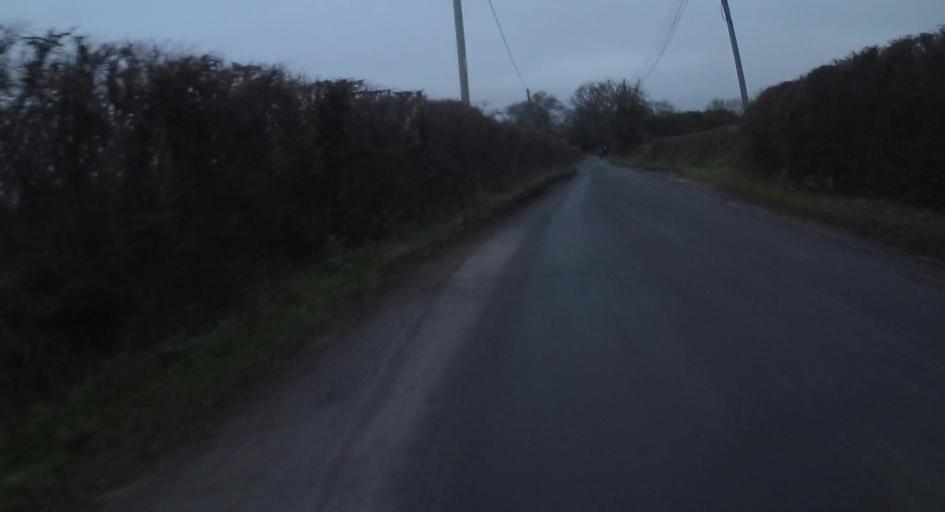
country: GB
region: England
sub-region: Hampshire
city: Tadley
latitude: 51.3340
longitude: -1.0921
